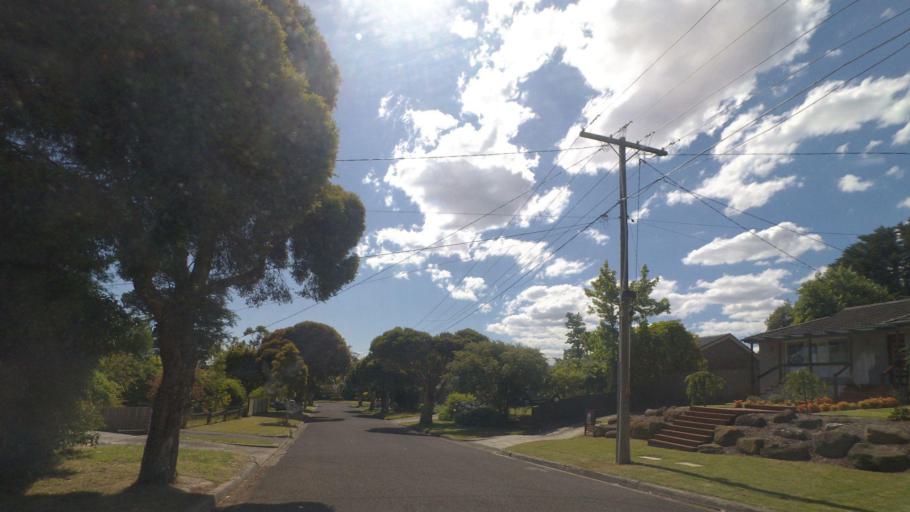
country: AU
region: Victoria
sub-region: Yarra Ranges
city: Kilsyth
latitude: -37.8026
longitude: 145.3289
